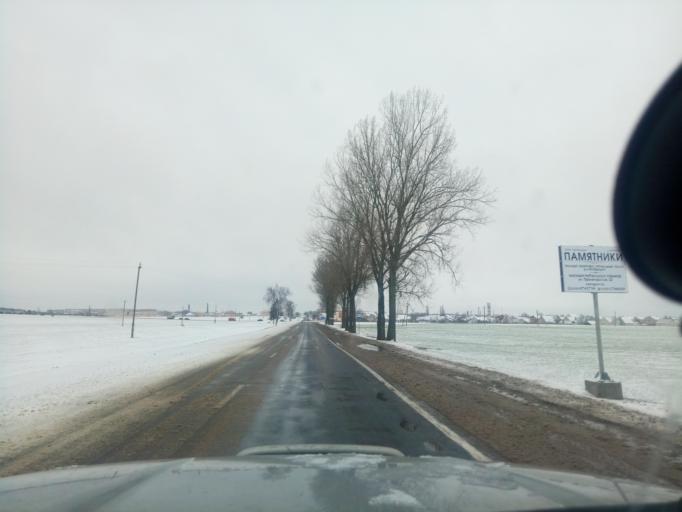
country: BY
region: Minsk
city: Kapyl'
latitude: 53.1345
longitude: 27.0849
